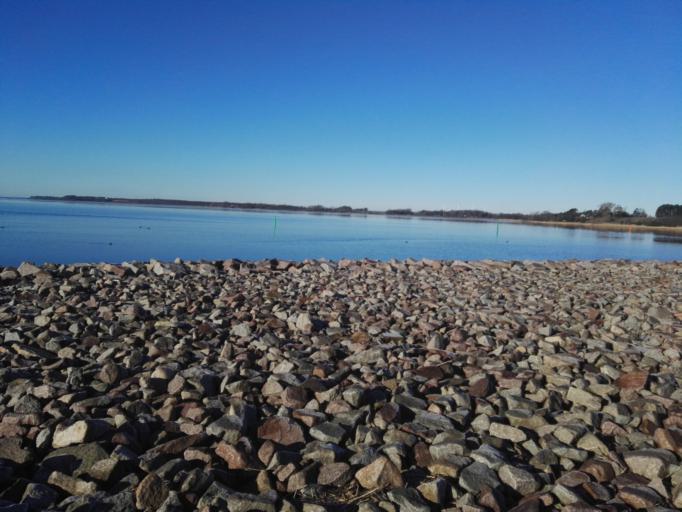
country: DK
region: Capital Region
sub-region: Halsnaes Kommune
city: Frederiksvaerk
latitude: 55.9612
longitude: 11.9983
